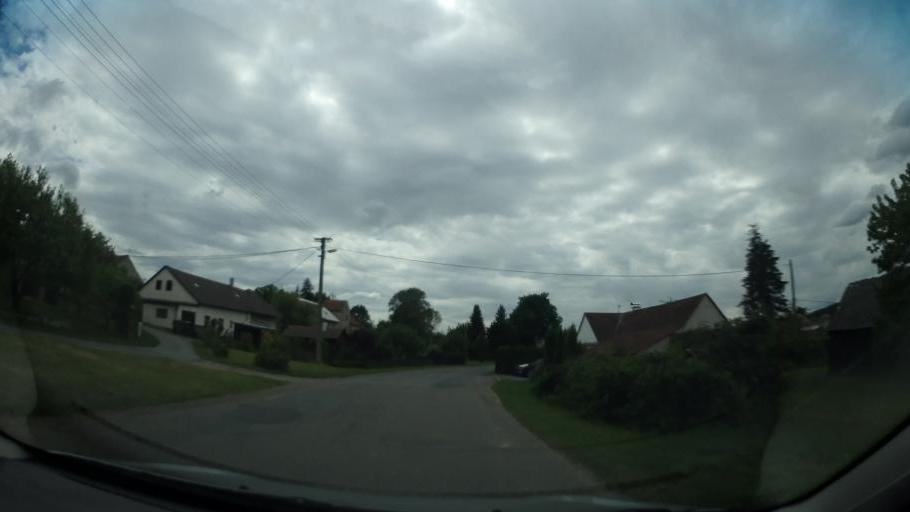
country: CZ
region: Pardubicky
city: Kuncina
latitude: 49.8406
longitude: 16.6979
